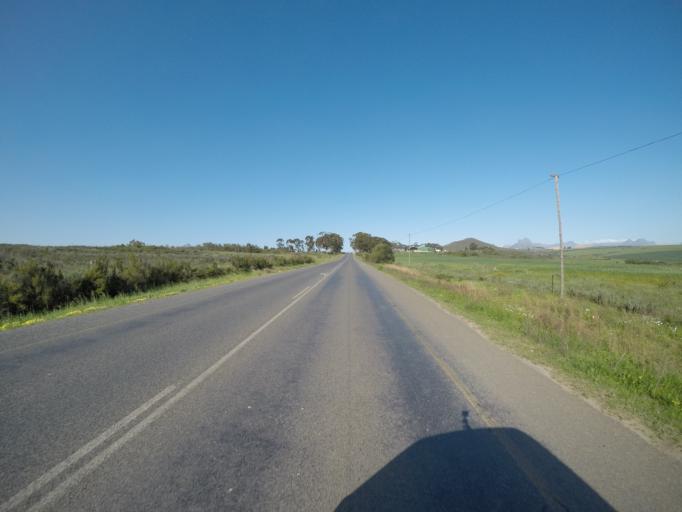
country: ZA
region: Western Cape
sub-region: City of Cape Town
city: Kraaifontein
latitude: -33.7644
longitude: 18.7679
